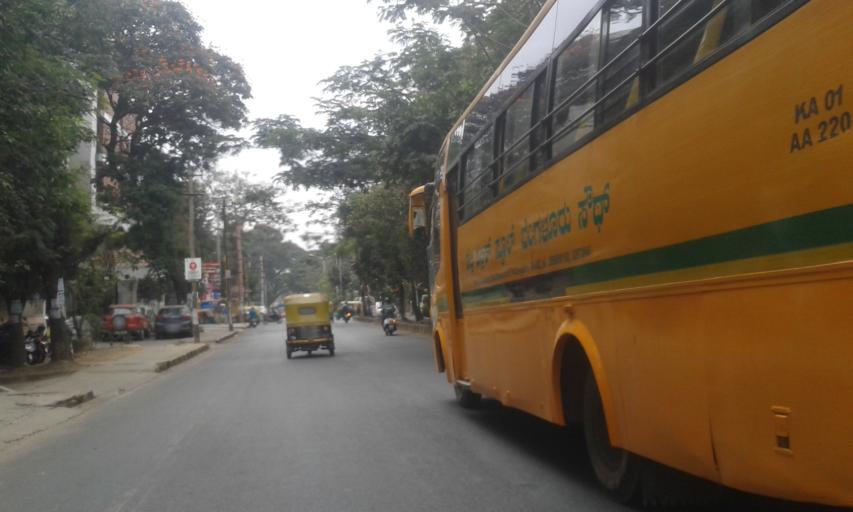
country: IN
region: Karnataka
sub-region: Bangalore Urban
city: Bangalore
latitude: 12.9064
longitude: 77.5792
